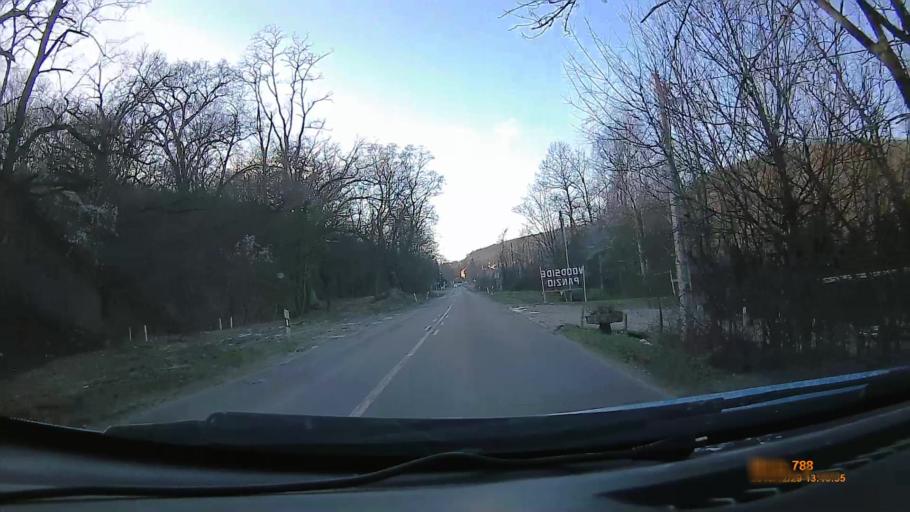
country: HU
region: Heves
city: Matraderecske
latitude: 47.9243
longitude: 20.0708
